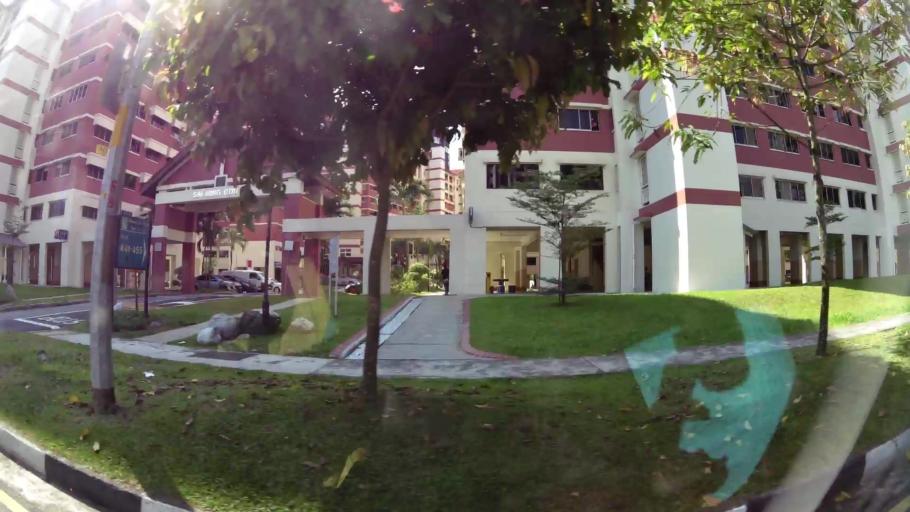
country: SG
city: Singapore
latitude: 1.3592
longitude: 103.8310
